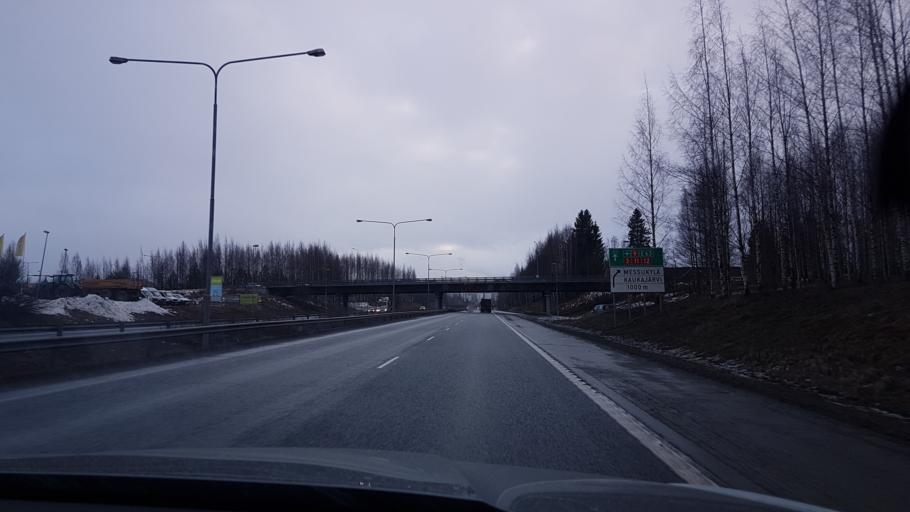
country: FI
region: Pirkanmaa
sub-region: Tampere
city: Tampere
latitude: 61.4900
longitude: 23.8745
